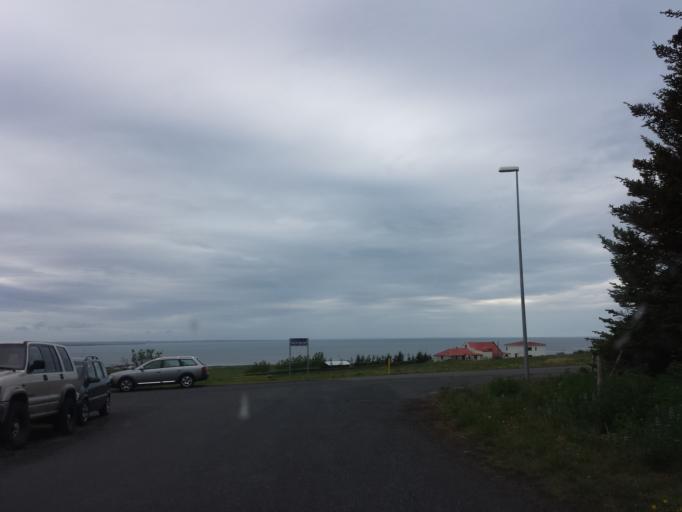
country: IS
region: Capital Region
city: Alftanes
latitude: 64.0860
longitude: -21.9920
